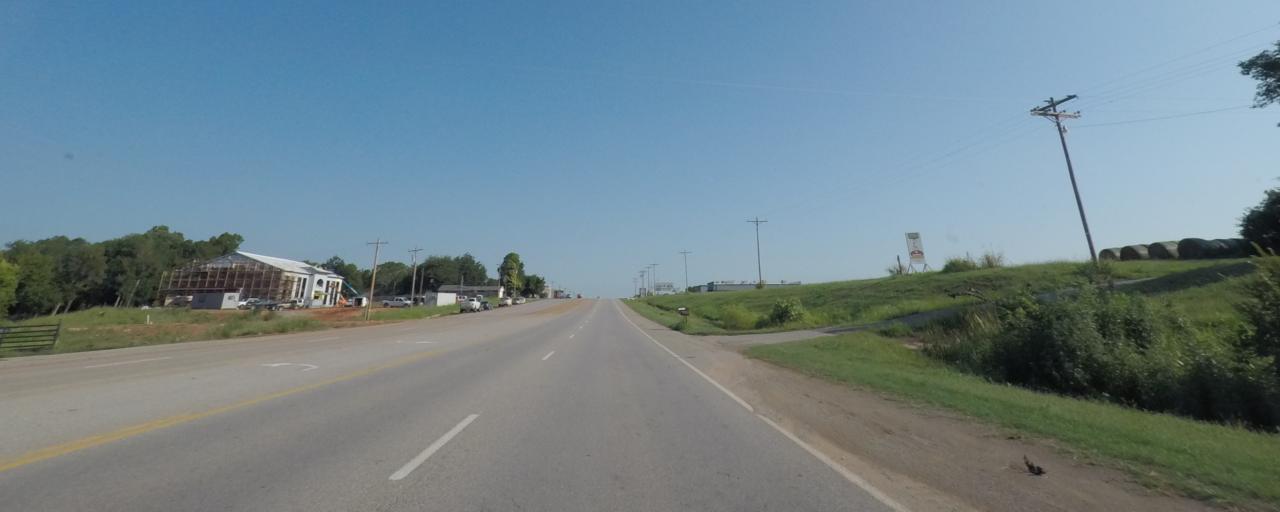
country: US
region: Oklahoma
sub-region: McClain County
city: Newcastle
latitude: 35.2689
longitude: -97.6001
